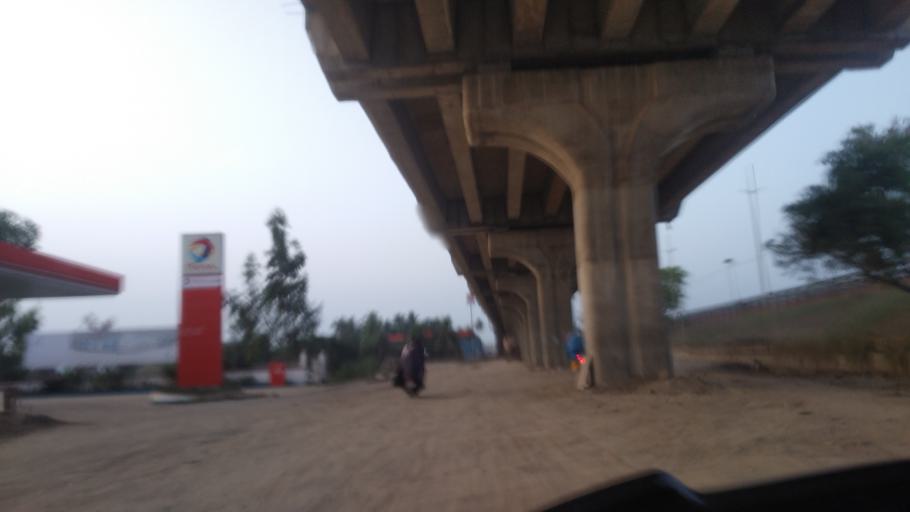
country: IN
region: Tamil Nadu
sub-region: Coimbatore
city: Coimbatore
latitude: 10.9831
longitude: 76.9616
